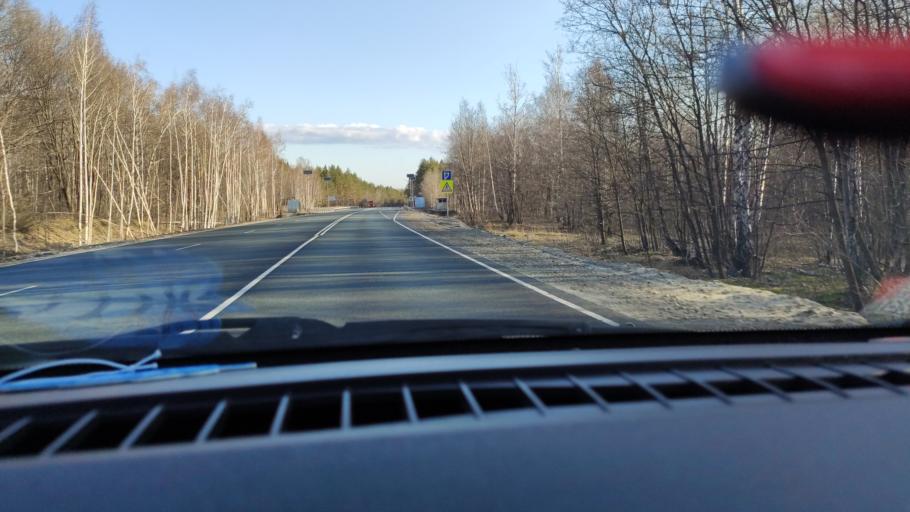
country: RU
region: Saratov
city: Khvalynsk
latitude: 52.5132
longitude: 48.0163
